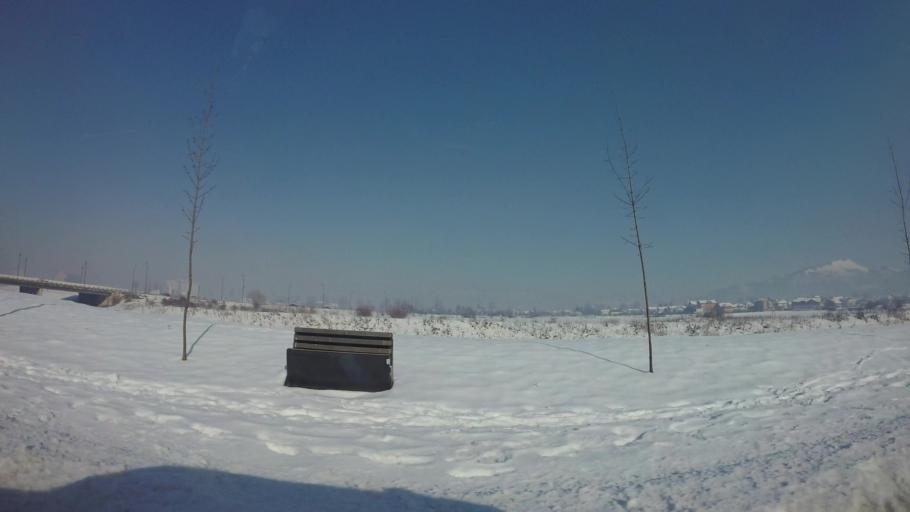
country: BA
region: Federation of Bosnia and Herzegovina
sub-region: Kanton Sarajevo
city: Sarajevo
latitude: 43.8190
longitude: 18.3128
